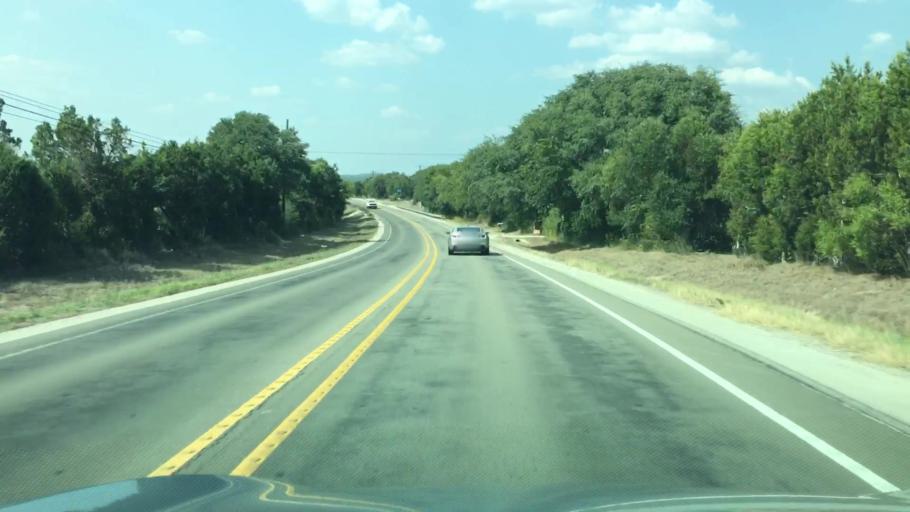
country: US
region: Texas
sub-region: Hays County
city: Dripping Springs
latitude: 30.1348
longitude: -98.0885
